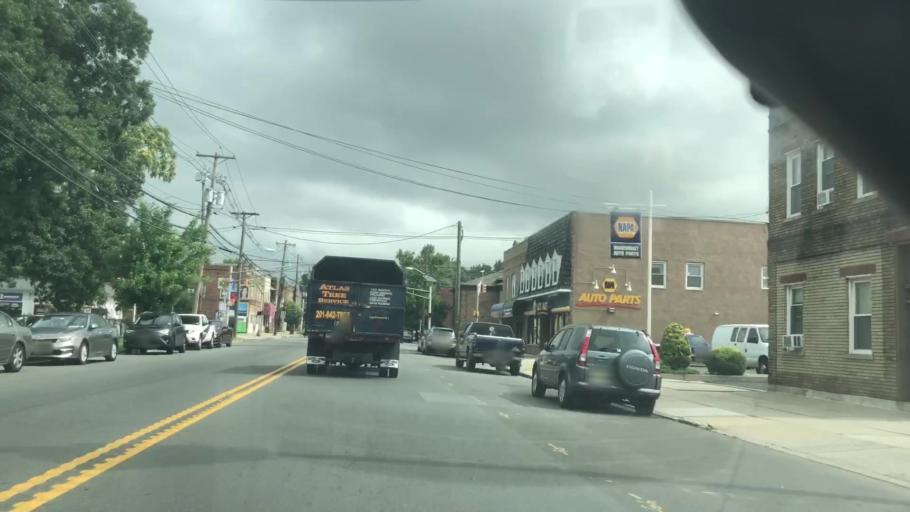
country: US
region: New Jersey
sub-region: Bergen County
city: Lyndhurst
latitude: 40.8111
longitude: -74.1167
